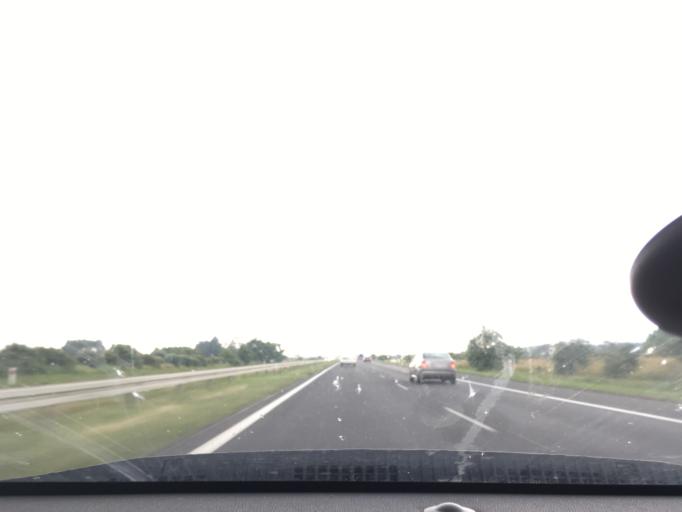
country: PL
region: Lodz Voivodeship
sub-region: Powiat radomszczanski
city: Kamiensk
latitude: 51.2254
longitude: 19.5050
